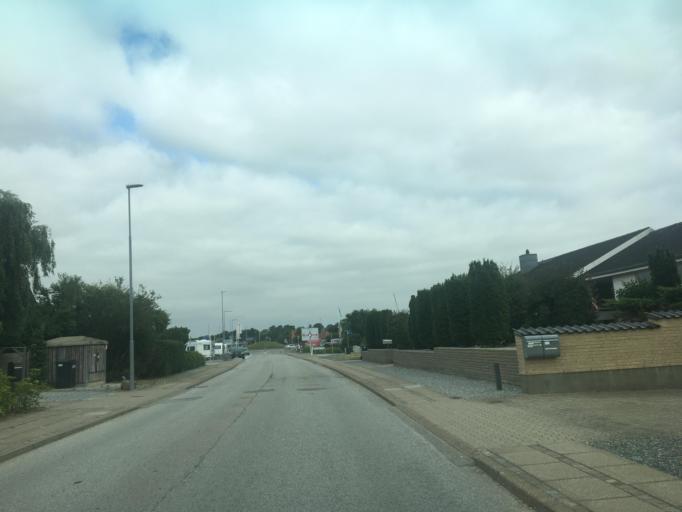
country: DK
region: North Denmark
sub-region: Thisted Kommune
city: Thisted
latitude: 56.8814
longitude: 8.6273
